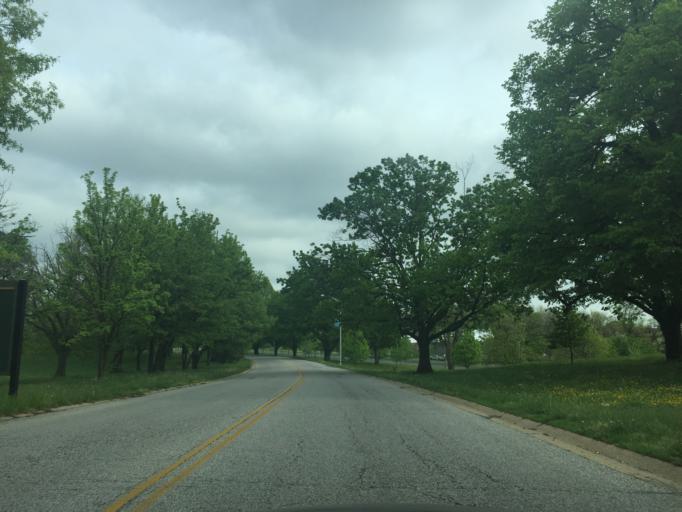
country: US
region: Maryland
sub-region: City of Baltimore
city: Baltimore
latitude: 39.3229
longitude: -76.6537
